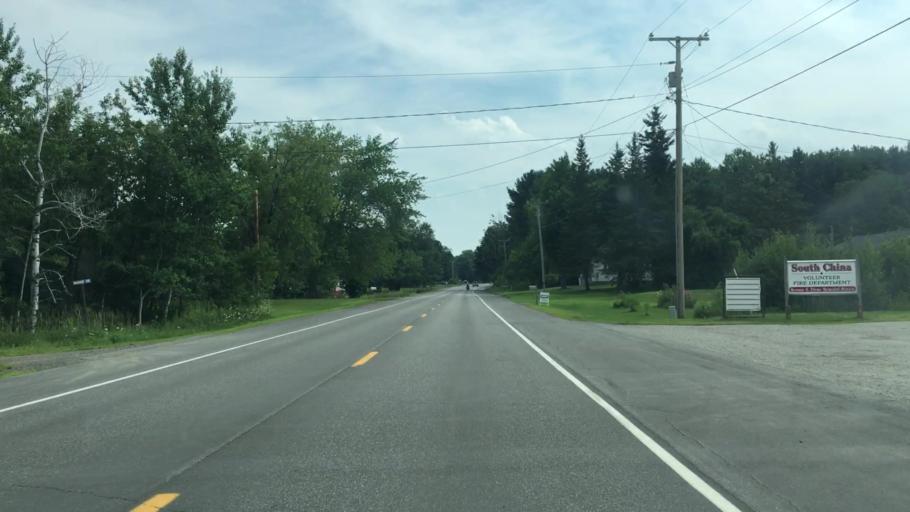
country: US
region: Maine
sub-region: Kennebec County
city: Windsor
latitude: 44.3908
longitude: -69.5707
